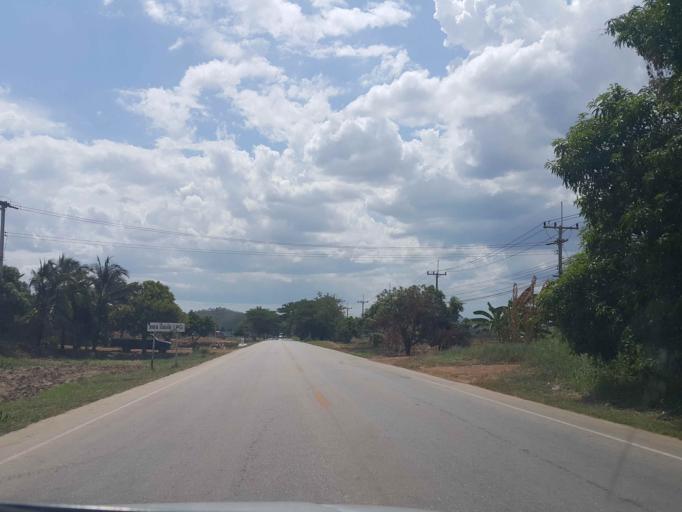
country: TH
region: Sukhothai
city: Thung Saliam
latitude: 17.3395
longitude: 99.6066
